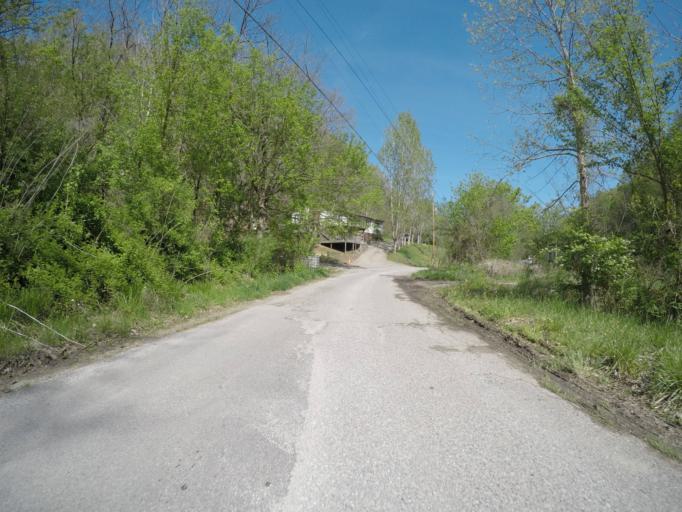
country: US
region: West Virginia
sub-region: Kanawha County
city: Charleston
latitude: 38.4183
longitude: -81.5875
